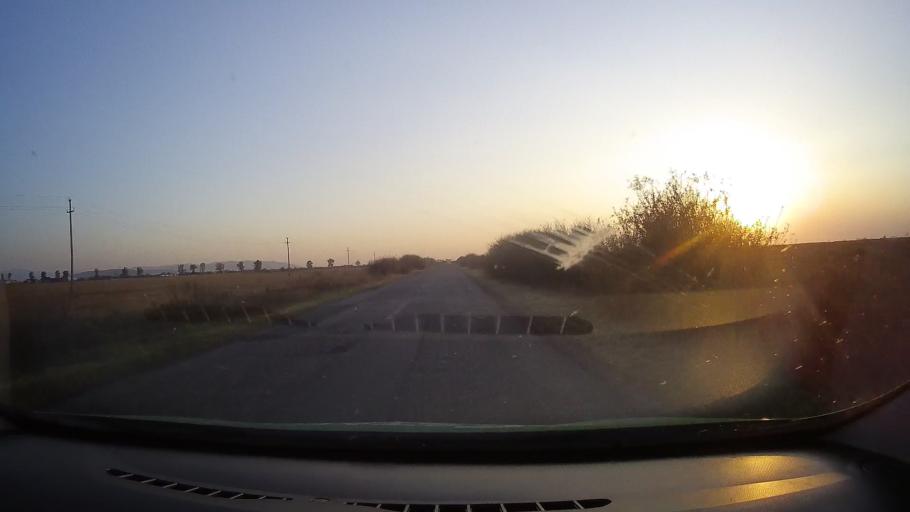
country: RO
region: Arad
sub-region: Comuna Seleus
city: Seleus
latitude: 46.3995
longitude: 21.7223
